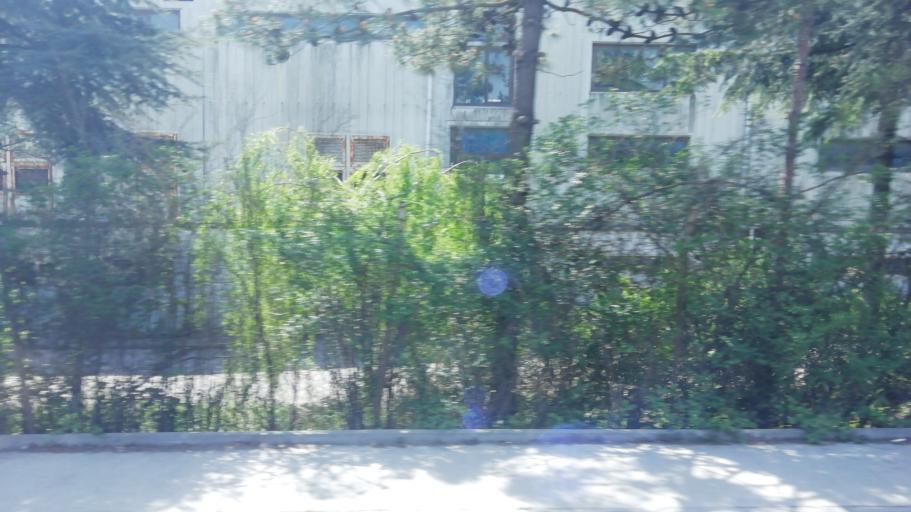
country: TR
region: Kocaeli
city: Gebze
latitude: 40.7978
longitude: 29.4504
